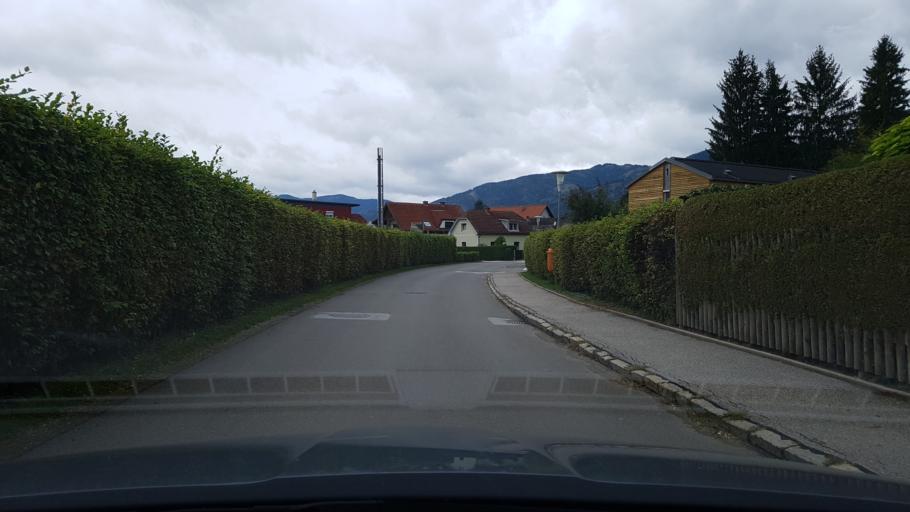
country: AT
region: Styria
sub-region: Politischer Bezirk Bruck-Muerzzuschlag
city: Sankt Marein im Muerztal
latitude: 47.4706
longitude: 15.3750
